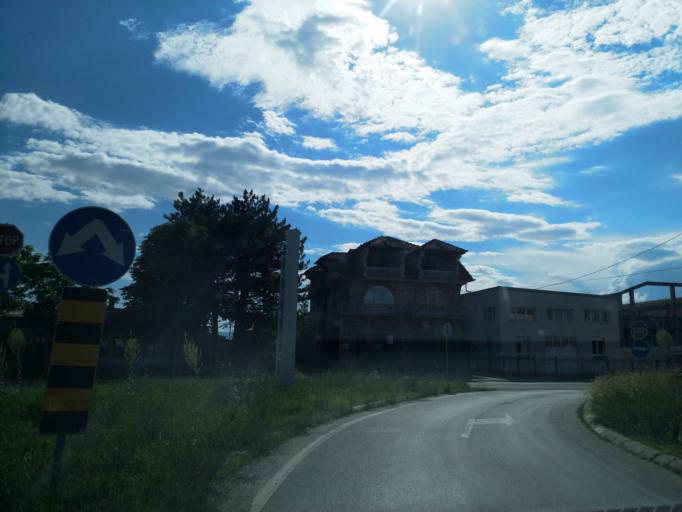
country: RS
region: Central Serbia
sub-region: Pomoravski Okrug
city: Paracin
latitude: 43.8522
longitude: 21.4101
